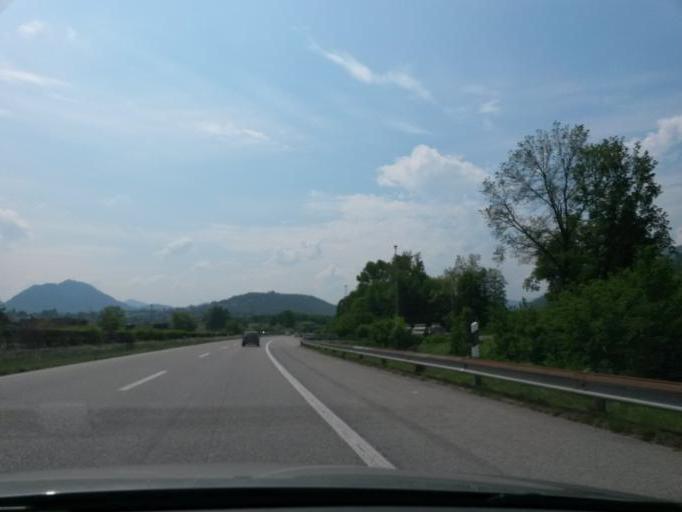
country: CH
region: Ticino
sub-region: Lugano District
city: Cadempino
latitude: 46.0376
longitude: 8.9292
